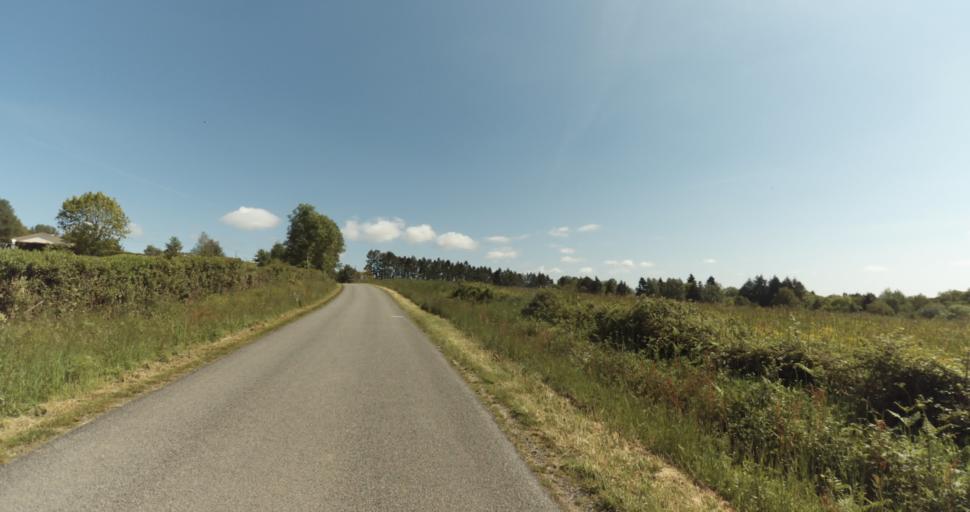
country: FR
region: Limousin
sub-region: Departement de la Haute-Vienne
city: Le Vigen
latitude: 45.7288
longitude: 1.2871
